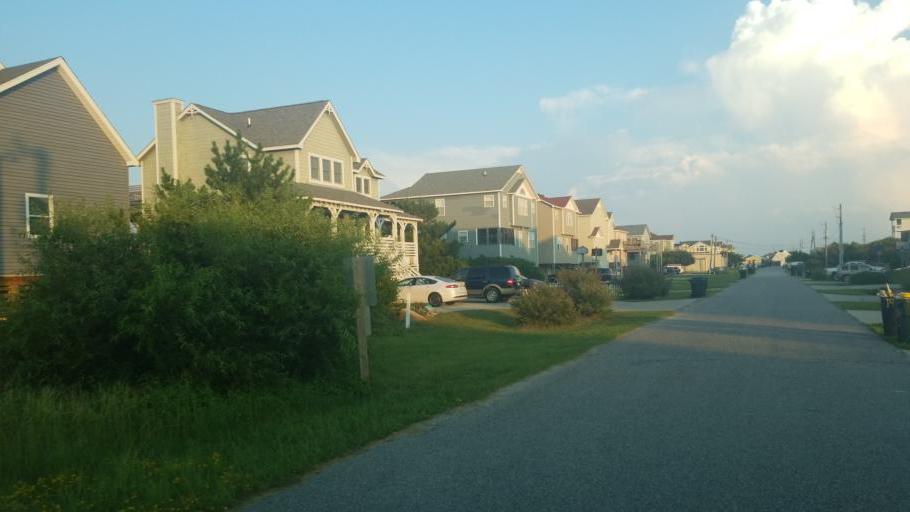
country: US
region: North Carolina
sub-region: Dare County
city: Kill Devil Hills
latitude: 36.0015
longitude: -75.6512
